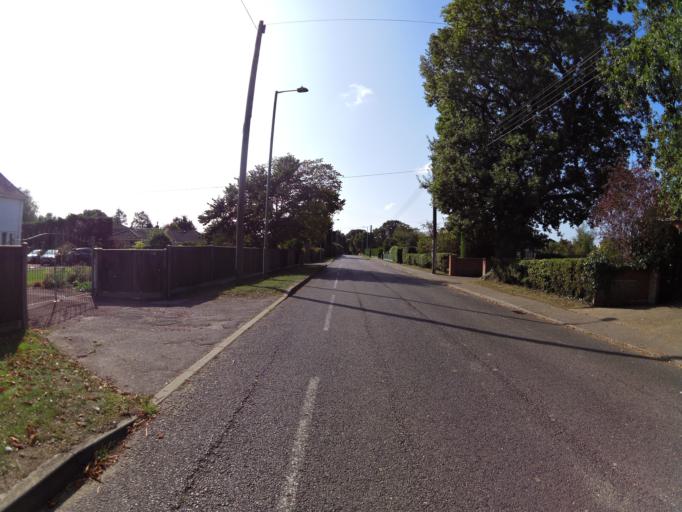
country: GB
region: England
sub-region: Suffolk
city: Kessingland
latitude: 52.4621
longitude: 1.7073
